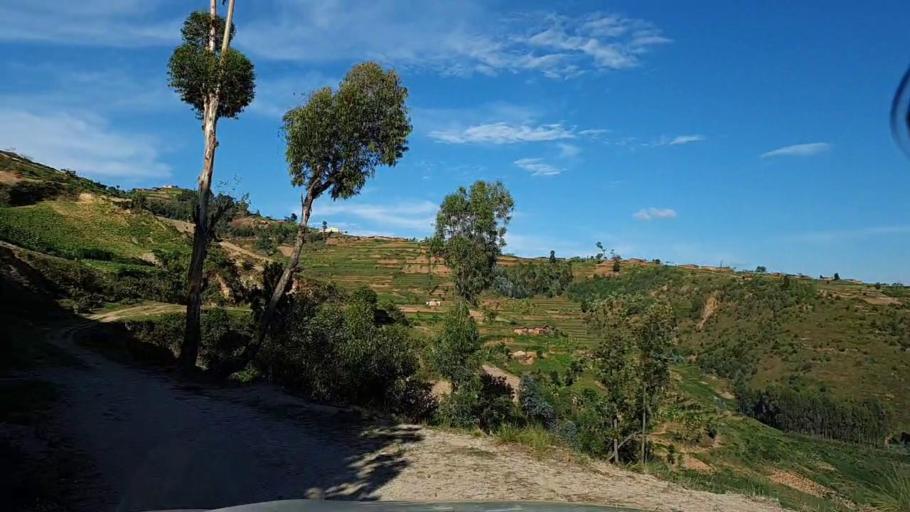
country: RW
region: Southern Province
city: Nzega
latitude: -2.4183
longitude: 29.5131
